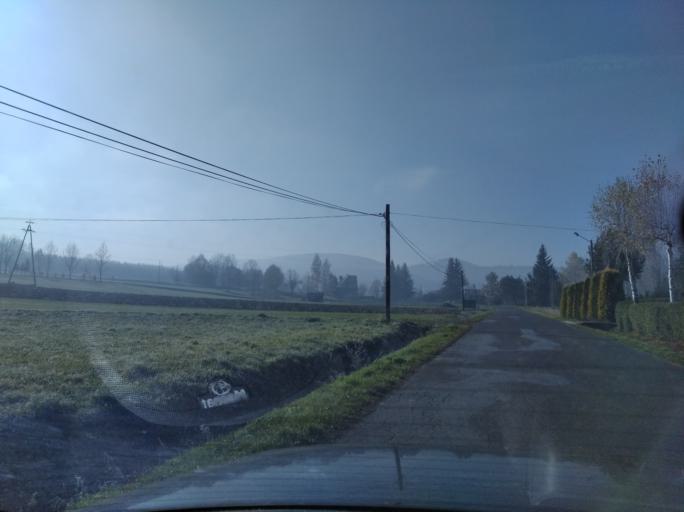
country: PL
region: Subcarpathian Voivodeship
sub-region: Powiat strzyzowski
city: Wysoka Strzyzowska
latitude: 49.8536
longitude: 21.7032
